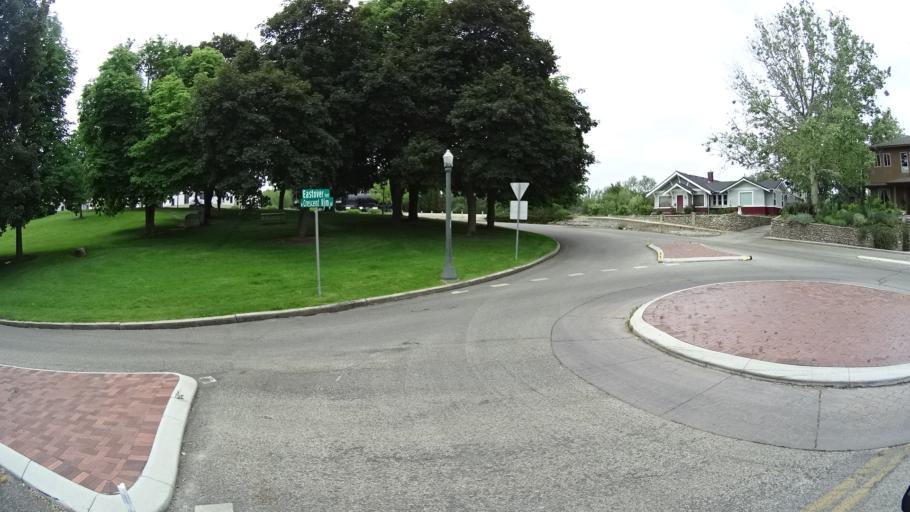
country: US
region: Idaho
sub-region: Ada County
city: Boise
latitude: 43.6031
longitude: -116.2152
